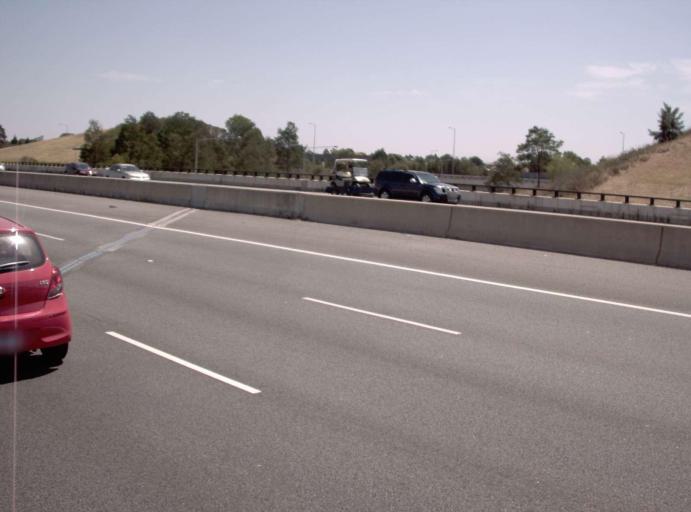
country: AU
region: Victoria
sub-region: Greater Dandenong
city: Noble Park North
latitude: -37.9448
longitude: 145.2040
